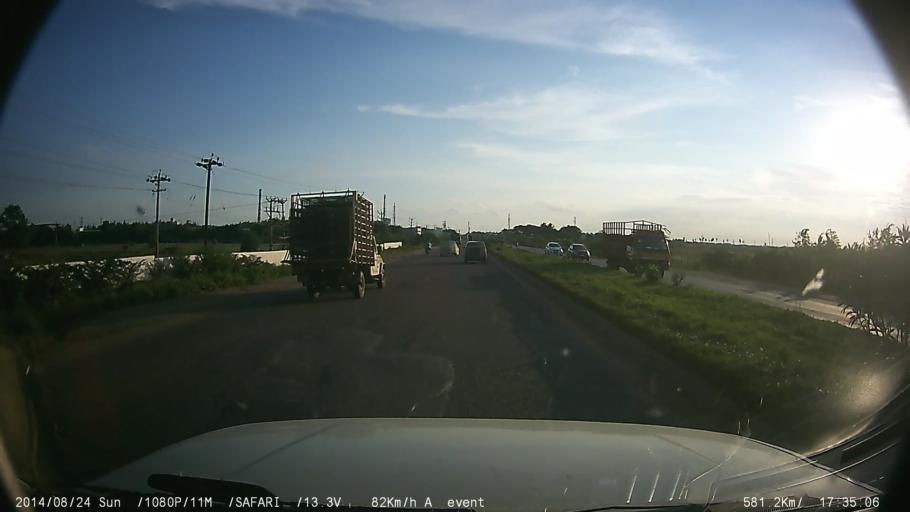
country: IN
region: Tamil Nadu
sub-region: Kancheepuram
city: Sriperumbudur
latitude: 12.9447
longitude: 79.9220
